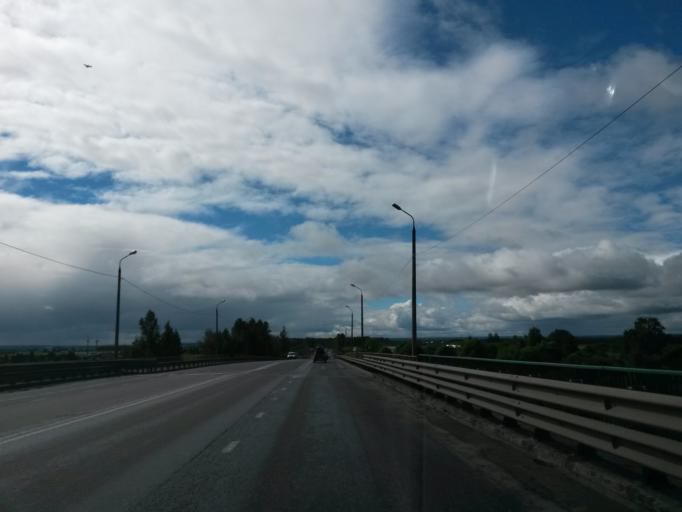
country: RU
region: Jaroslavl
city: Yaroslavl
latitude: 57.6668
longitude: 39.7655
